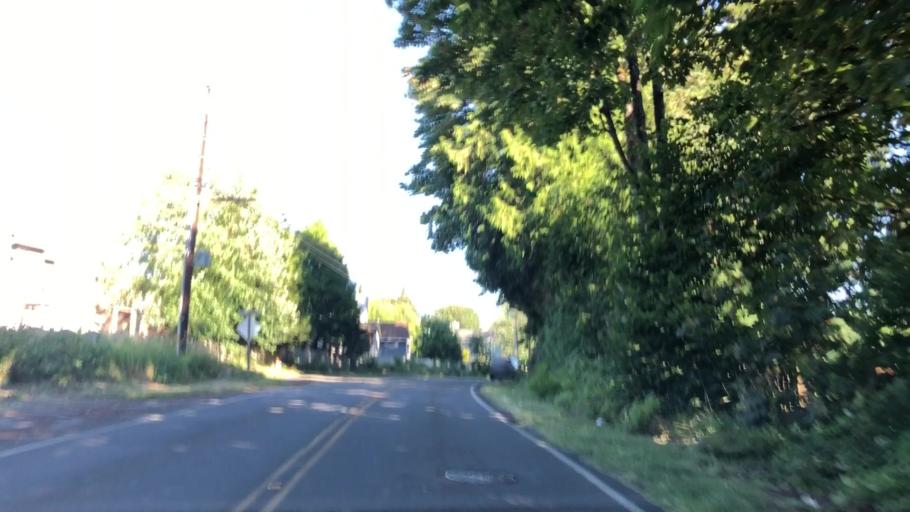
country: US
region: Washington
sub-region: Snohomish County
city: Brier
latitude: 47.8056
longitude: -122.2431
